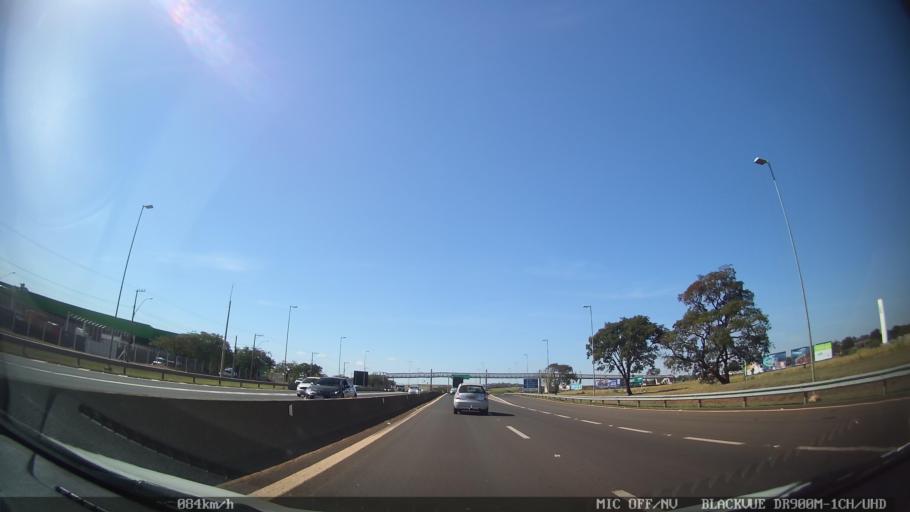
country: BR
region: Sao Paulo
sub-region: Ribeirao Preto
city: Ribeirao Preto
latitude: -21.2082
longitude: -47.7635
